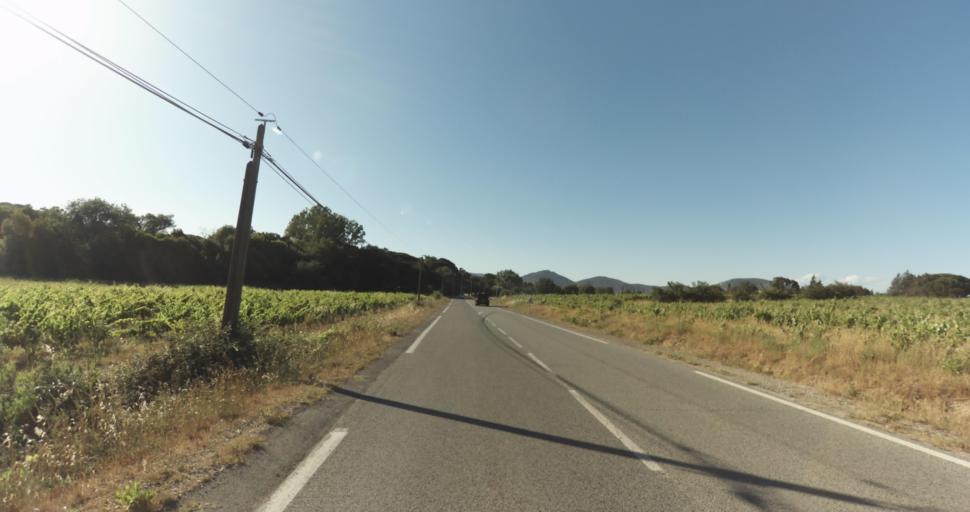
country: FR
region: Provence-Alpes-Cote d'Azur
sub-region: Departement du Var
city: Gassin
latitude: 43.2487
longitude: 6.5935
